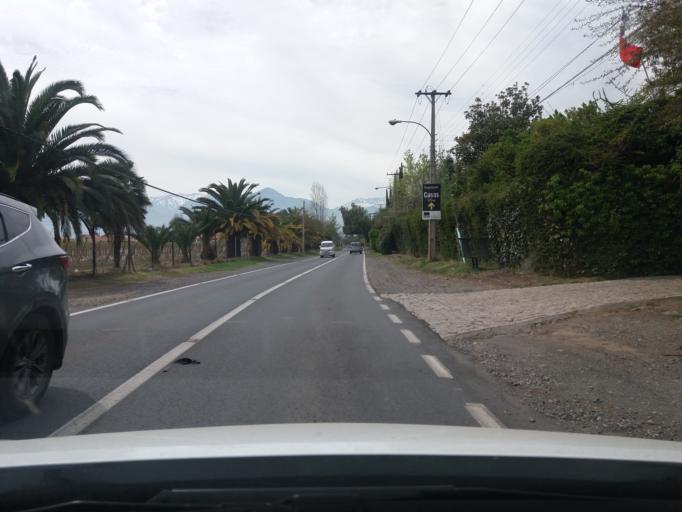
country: CL
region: Valparaiso
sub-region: Provincia de Los Andes
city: Los Andes
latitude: -32.8323
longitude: -70.6253
